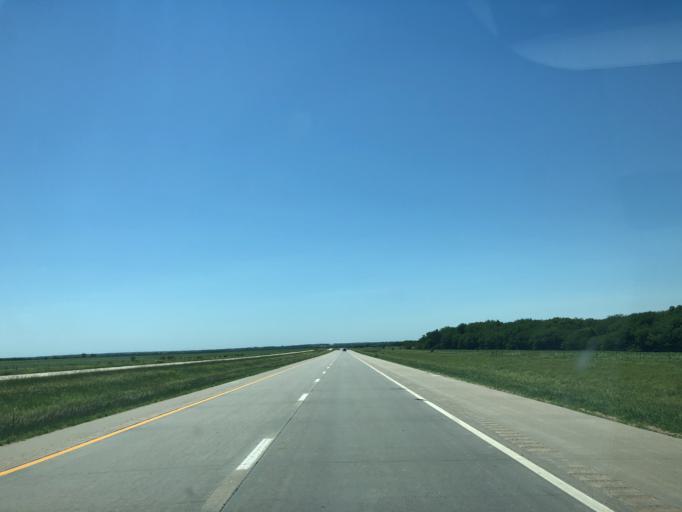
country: US
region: Kansas
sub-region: Cloud County
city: Concordia
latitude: 39.6351
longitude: -97.6605
